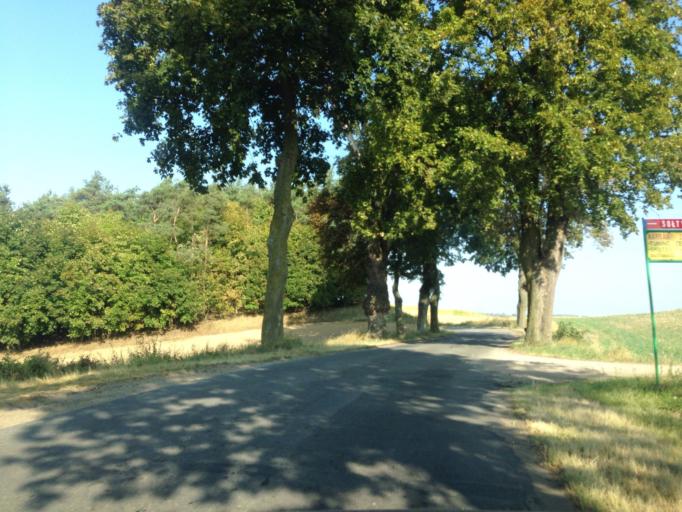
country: PL
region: Kujawsko-Pomorskie
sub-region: Powiat brodnicki
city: Brzozie
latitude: 53.2991
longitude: 19.6267
